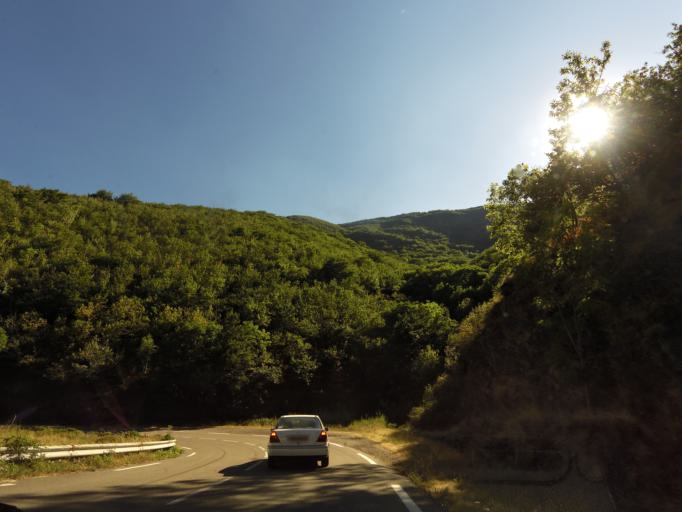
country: FR
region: Languedoc-Roussillon
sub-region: Departement du Gard
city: Valleraugue
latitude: 44.0891
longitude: 3.5822
